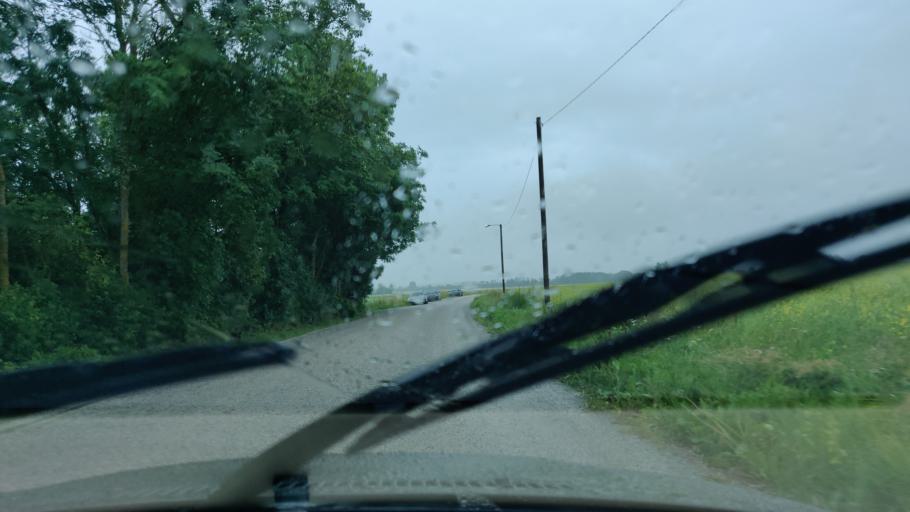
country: EE
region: Jaervamaa
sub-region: Jaerva-Jaani vald
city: Jarva-Jaani
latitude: 59.0939
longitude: 25.6993
